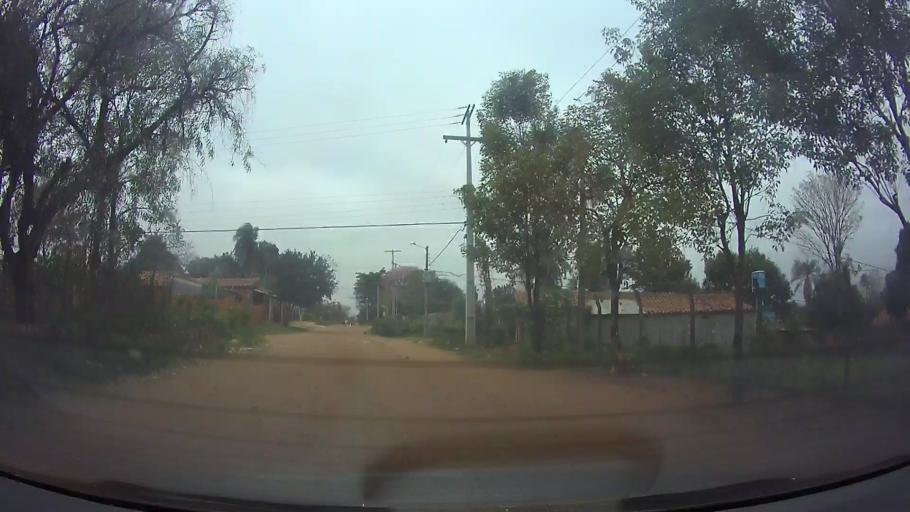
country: PY
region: Central
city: Limpio
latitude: -25.1536
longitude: -57.4560
